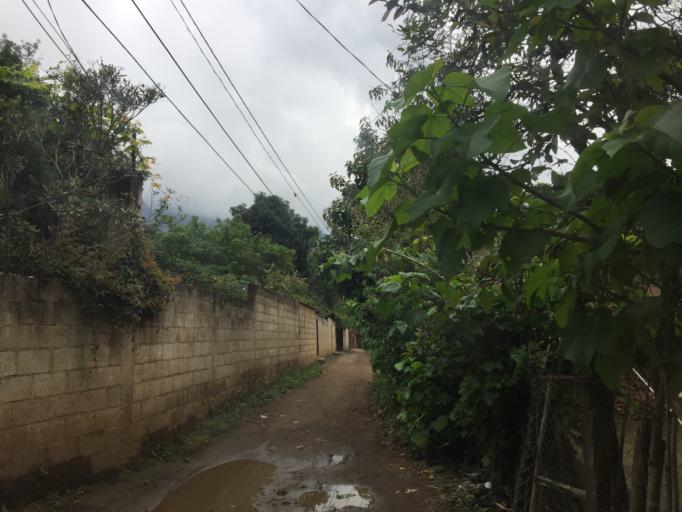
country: GT
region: Sacatepequez
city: Magdalena Milpas Altas
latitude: 14.5106
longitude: -90.6546
